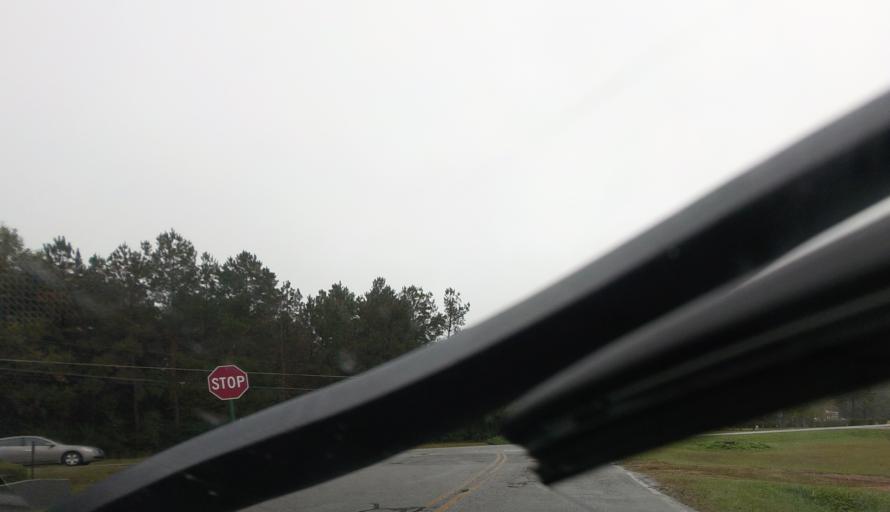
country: US
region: Georgia
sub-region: Peach County
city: Fort Valley
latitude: 32.5441
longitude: -83.9034
